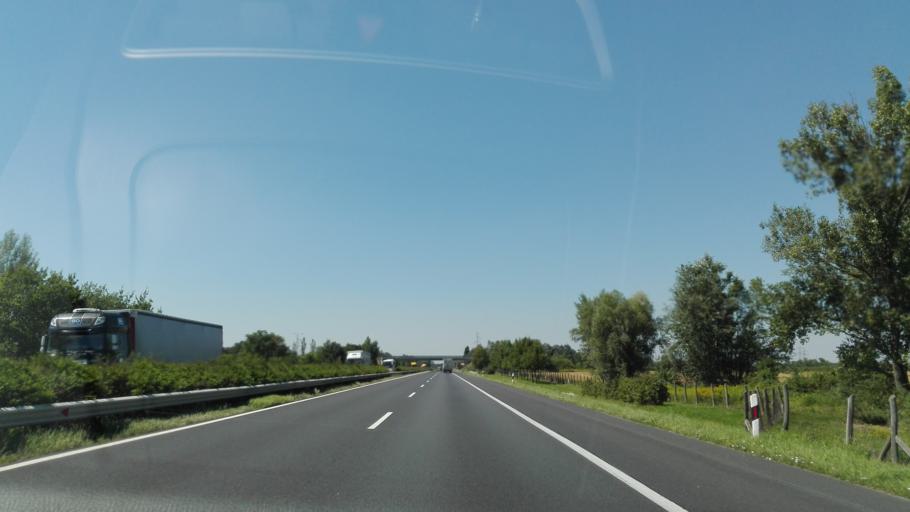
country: HU
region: Gyor-Moson-Sopron
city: Lebeny
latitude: 47.7701
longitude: 17.3751
